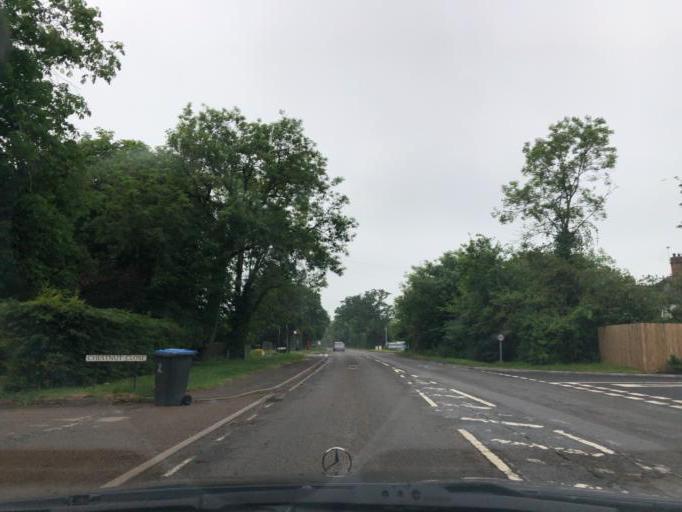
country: GB
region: England
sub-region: Warwickshire
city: Harbury
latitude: 52.2001
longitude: -1.4853
